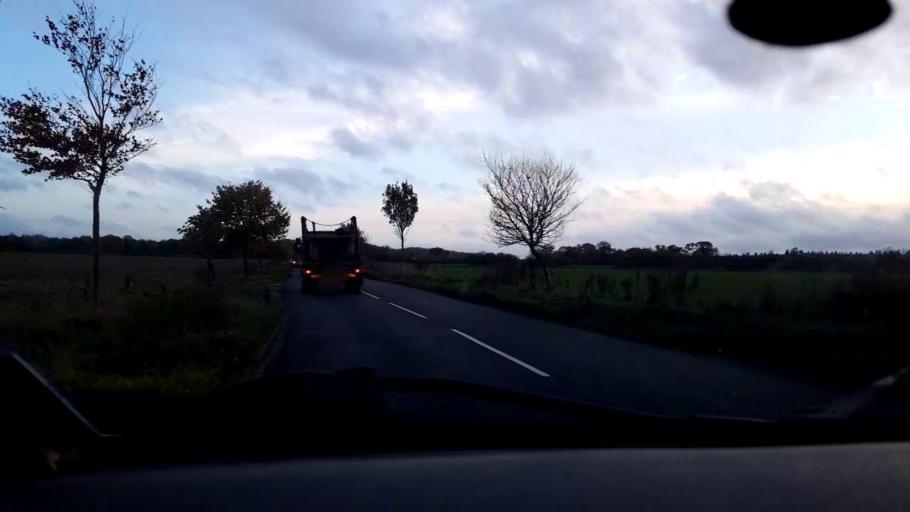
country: GB
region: England
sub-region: Norfolk
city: Mattishall
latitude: 52.7005
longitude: 1.0991
